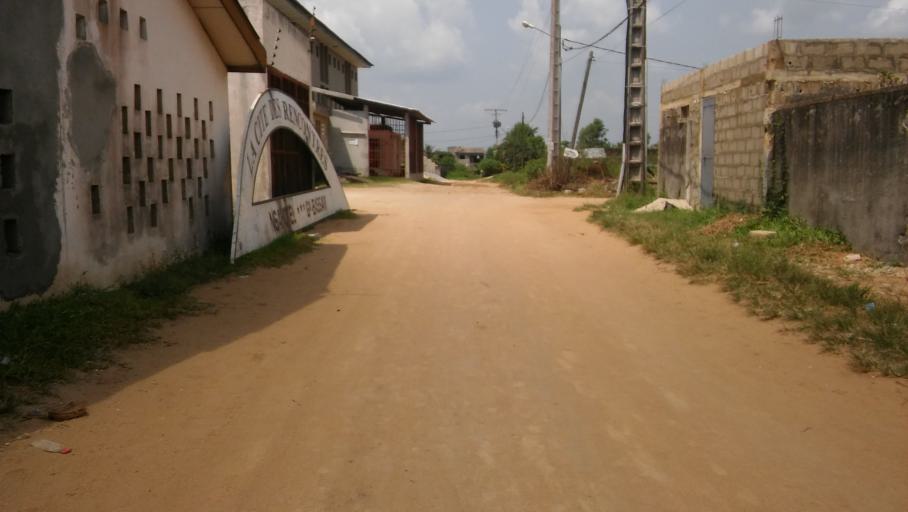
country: CI
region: Sud-Comoe
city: Grand-Bassam
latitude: 5.2182
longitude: -3.7413
